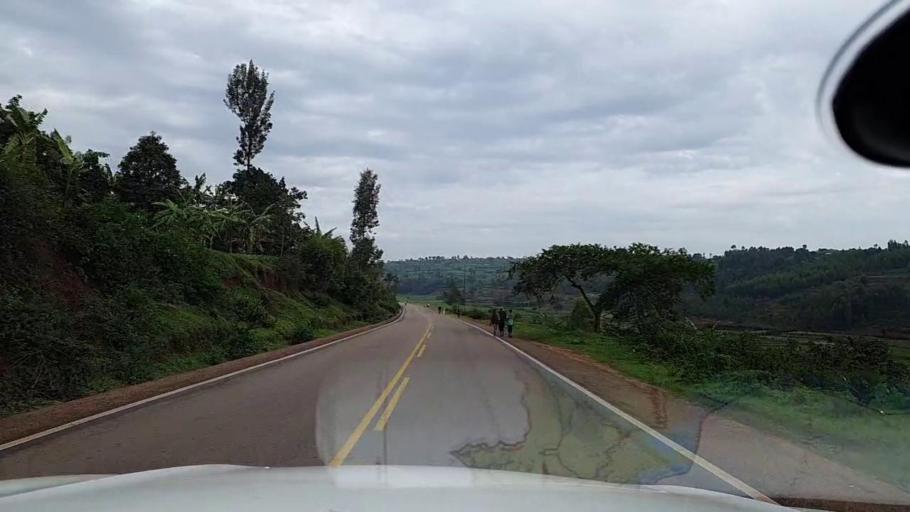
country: RW
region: Southern Province
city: Butare
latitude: -2.5748
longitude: 29.7333
